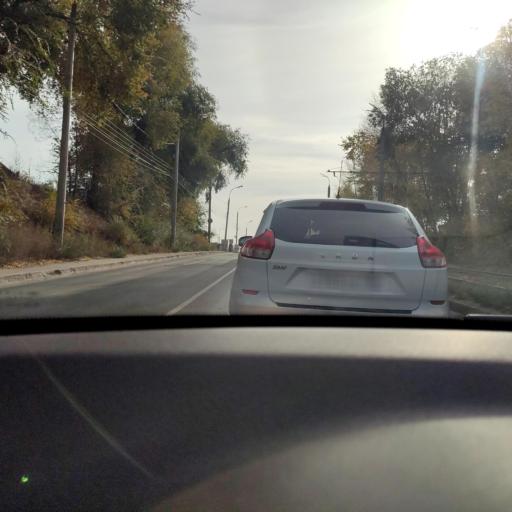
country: RU
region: Samara
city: Smyshlyayevka
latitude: 53.2251
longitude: 50.2842
